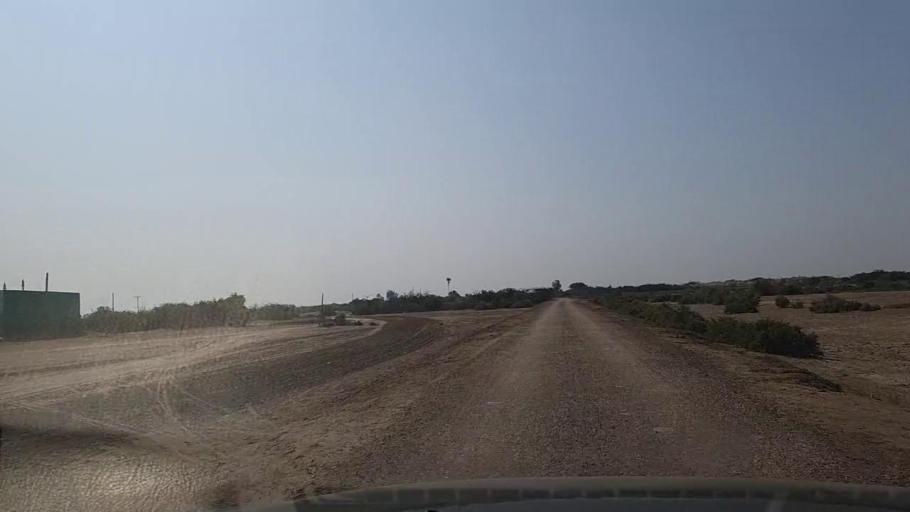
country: PK
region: Sindh
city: Mirpur Sakro
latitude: 24.4251
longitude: 67.7082
